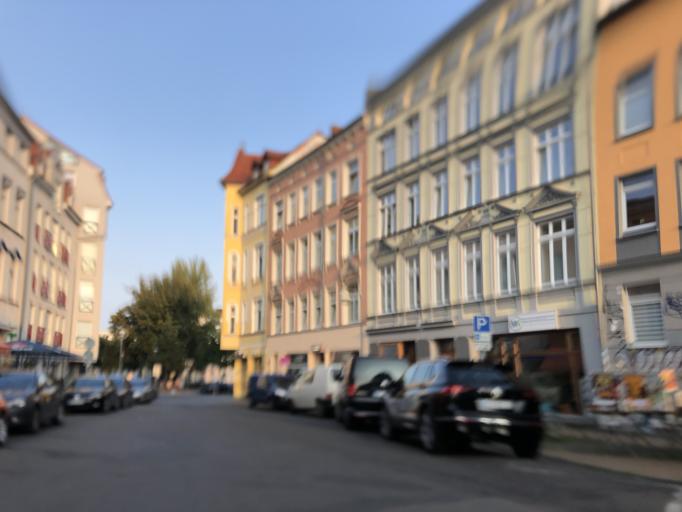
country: DE
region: Mecklenburg-Vorpommern
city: Rostock
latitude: 54.0880
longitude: 12.1203
